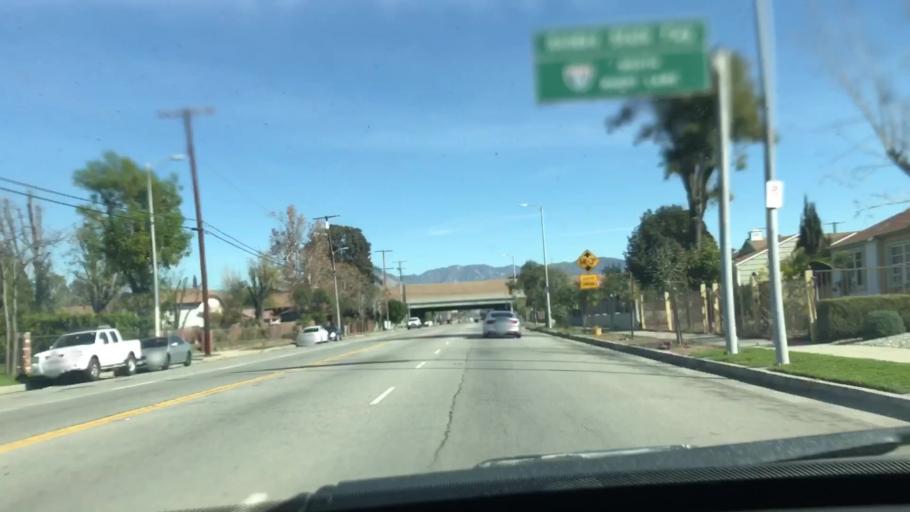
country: US
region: California
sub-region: Los Angeles County
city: San Fernando
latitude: 34.2373
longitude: -118.4181
